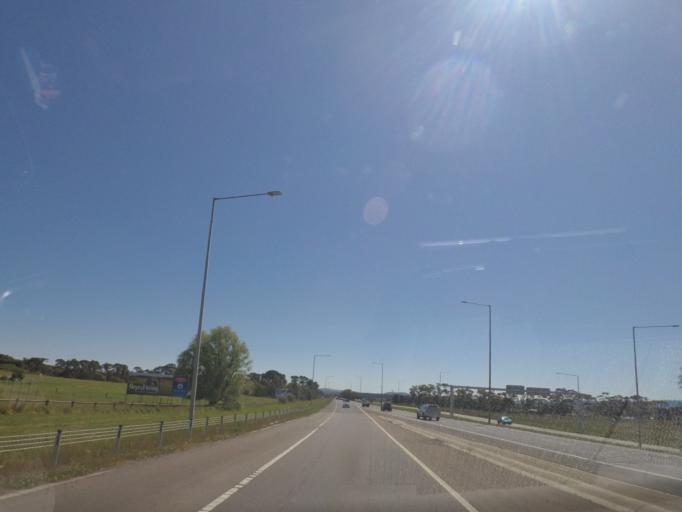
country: AU
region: Victoria
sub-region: Hume
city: Craigieburn
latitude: -37.5669
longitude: 144.9410
